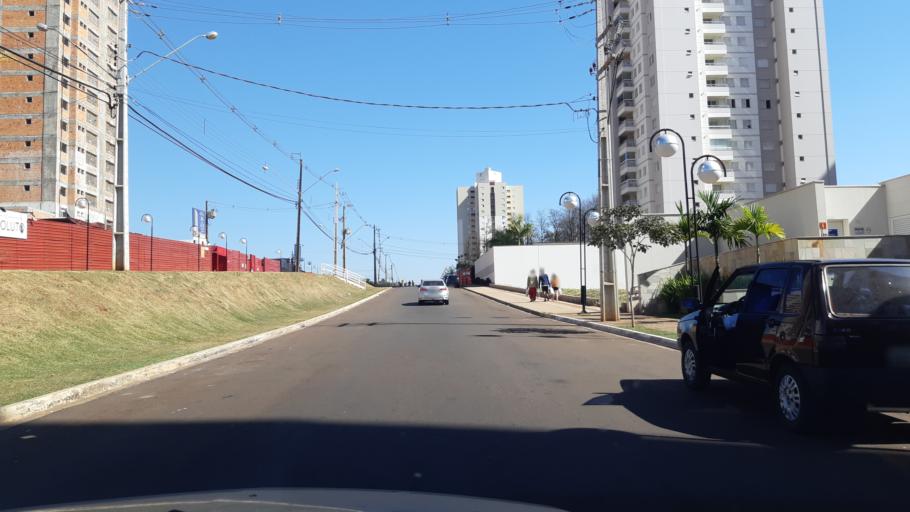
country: BR
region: Parana
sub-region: Londrina
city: Londrina
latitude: -23.3304
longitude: -51.1816
